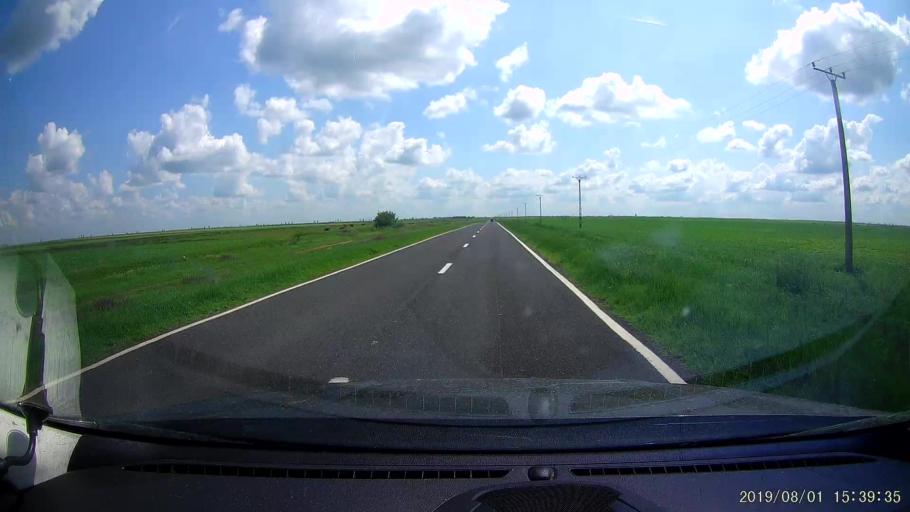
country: RO
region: Braila
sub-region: Comuna Baraganul
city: Baraganul
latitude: 44.8540
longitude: 27.5565
